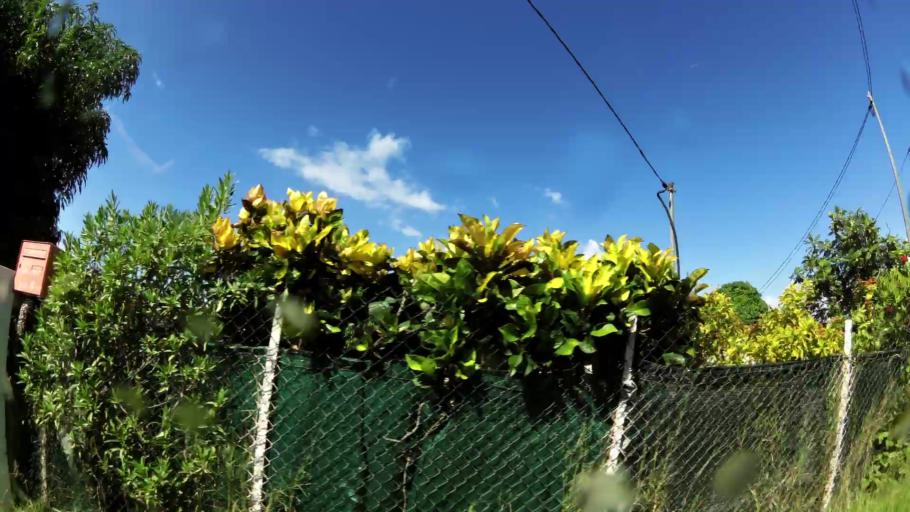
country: MQ
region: Martinique
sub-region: Martinique
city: Les Trois-Ilets
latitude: 14.4628
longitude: -61.0666
